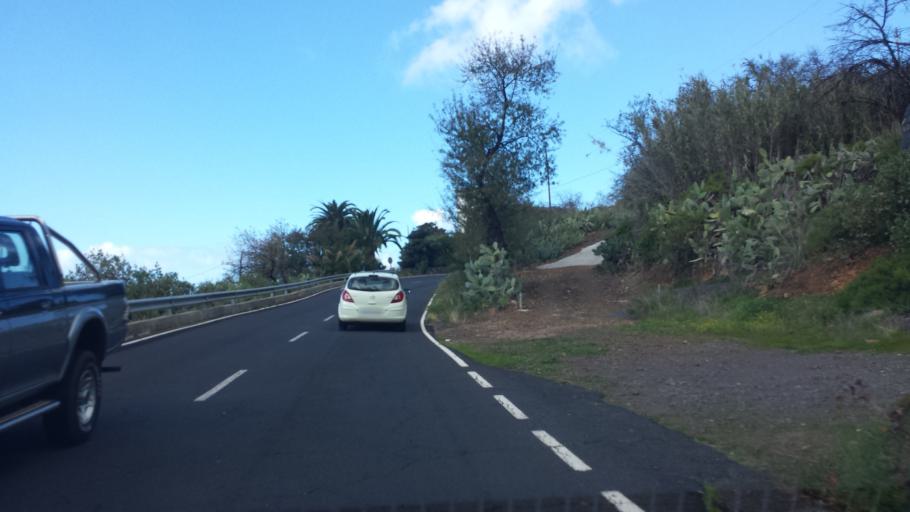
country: ES
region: Canary Islands
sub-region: Provincia de Santa Cruz de Tenerife
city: Tijarafe
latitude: 28.7230
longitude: -17.9581
